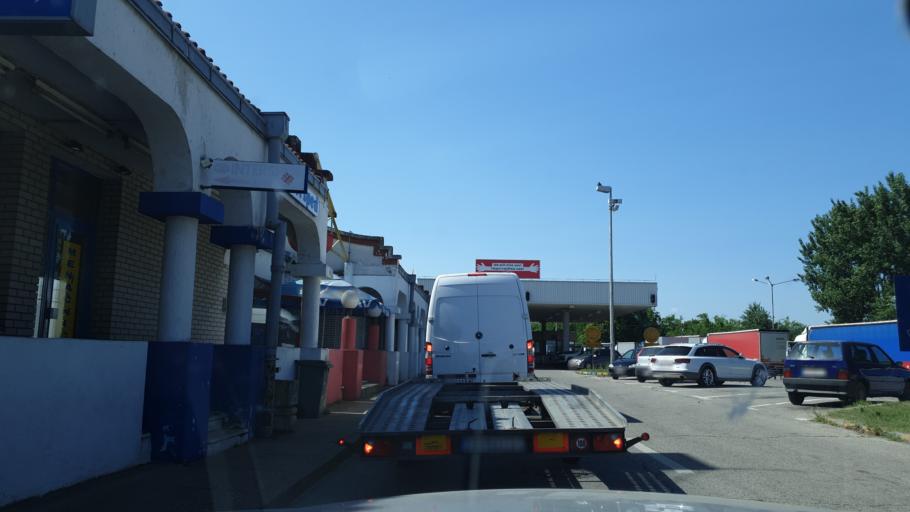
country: HU
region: Bacs-Kiskun
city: Tompa
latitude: 46.1666
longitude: 19.5619
